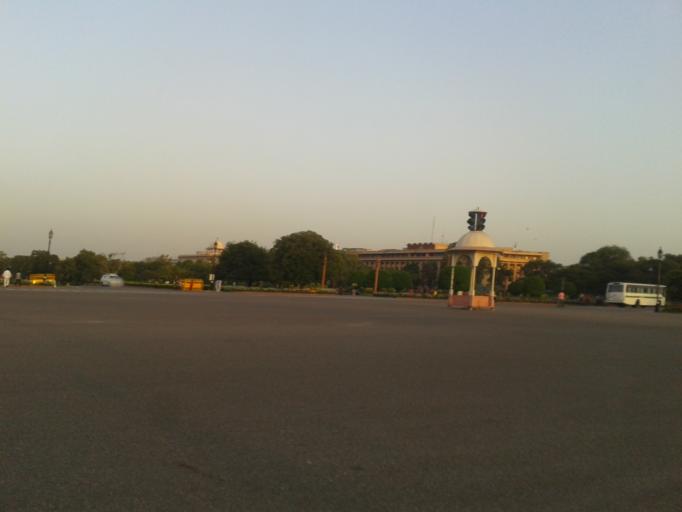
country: IN
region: NCT
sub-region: New Delhi
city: New Delhi
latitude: 28.6142
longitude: 77.2088
